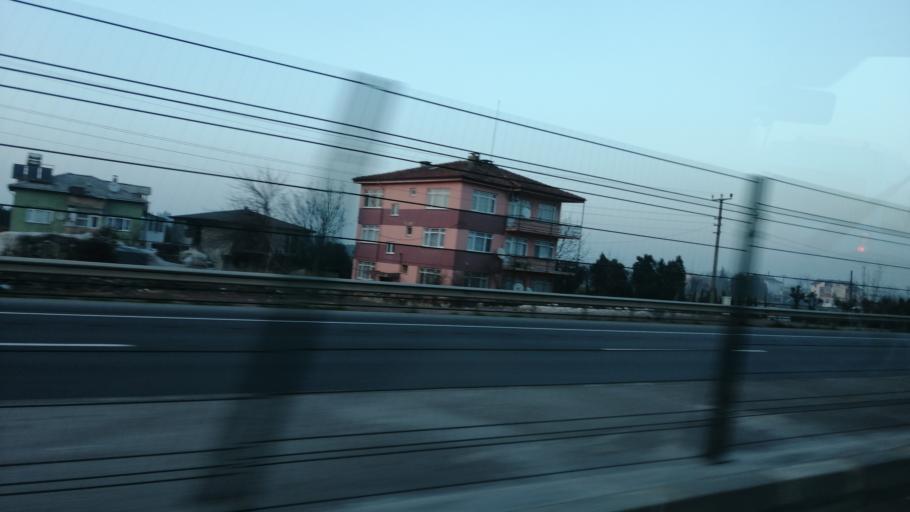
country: TR
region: Yalova
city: Altinova
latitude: 40.6881
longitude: 29.4578
